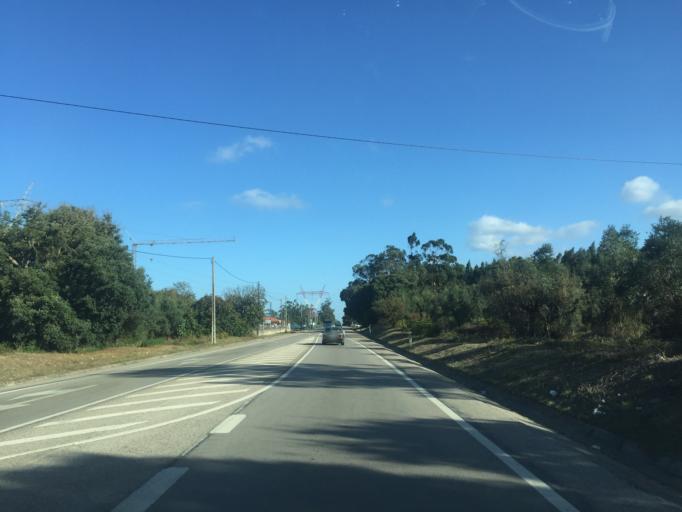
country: PT
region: Leiria
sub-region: Alcobaca
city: Turquel
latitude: 39.4654
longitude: -8.9433
